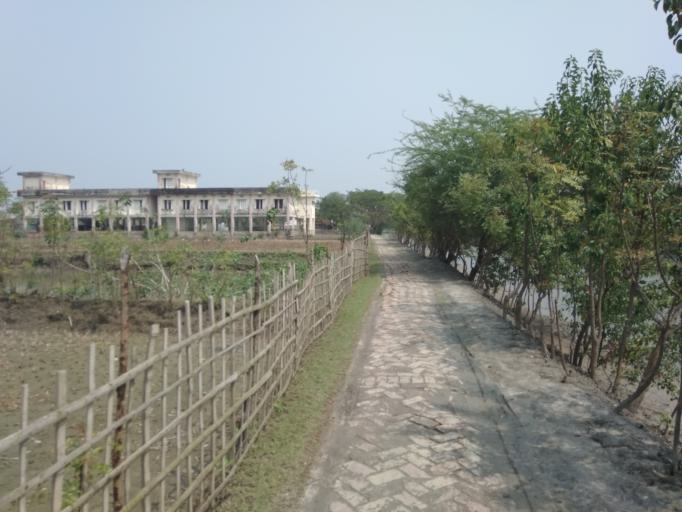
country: IN
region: West Bengal
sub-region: North 24 Parganas
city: Taki
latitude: 22.2589
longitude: 89.2588
